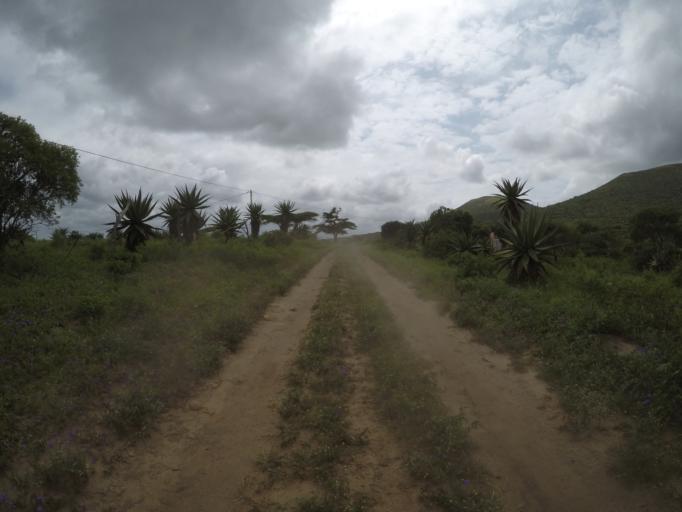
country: ZA
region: KwaZulu-Natal
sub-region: uThungulu District Municipality
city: Empangeni
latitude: -28.5800
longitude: 31.8693
